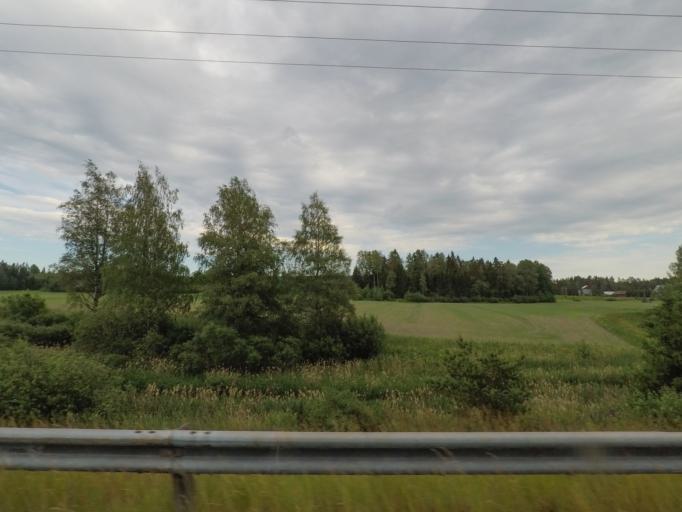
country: FI
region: Uusimaa
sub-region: Helsinki
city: Maentsaelae
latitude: 60.6888
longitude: 25.3733
